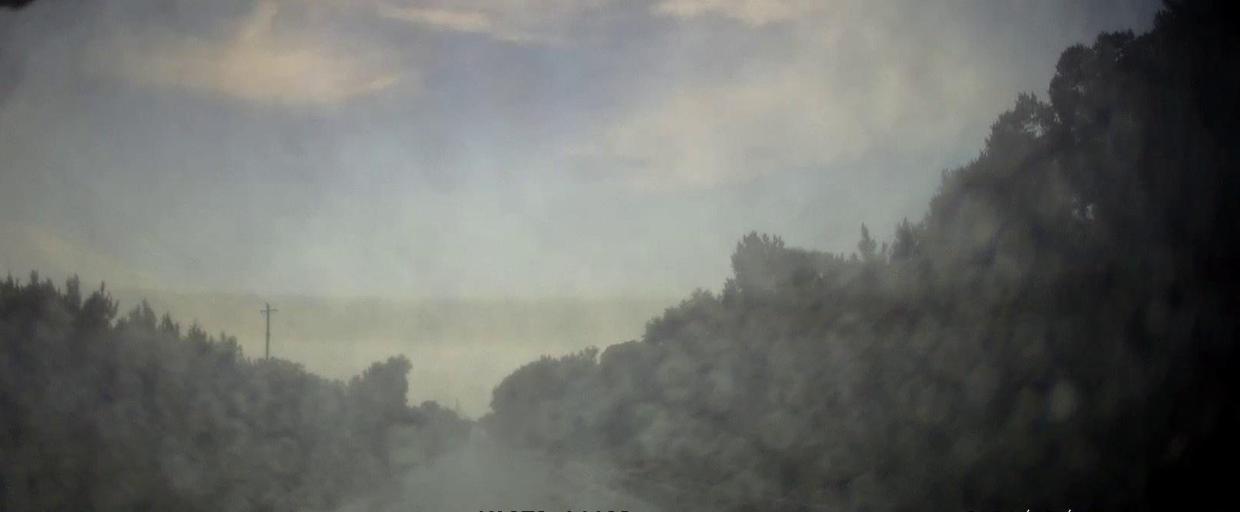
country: US
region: Georgia
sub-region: Dodge County
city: Chester
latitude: 32.5618
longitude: -83.1605
